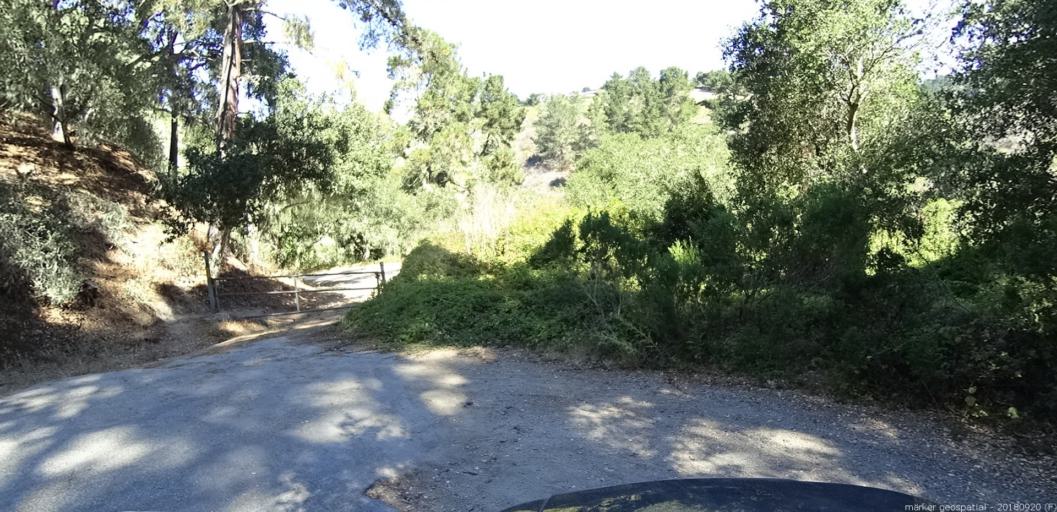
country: US
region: California
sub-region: Monterey County
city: Carmel-by-the-Sea
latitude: 36.5579
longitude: -121.9076
